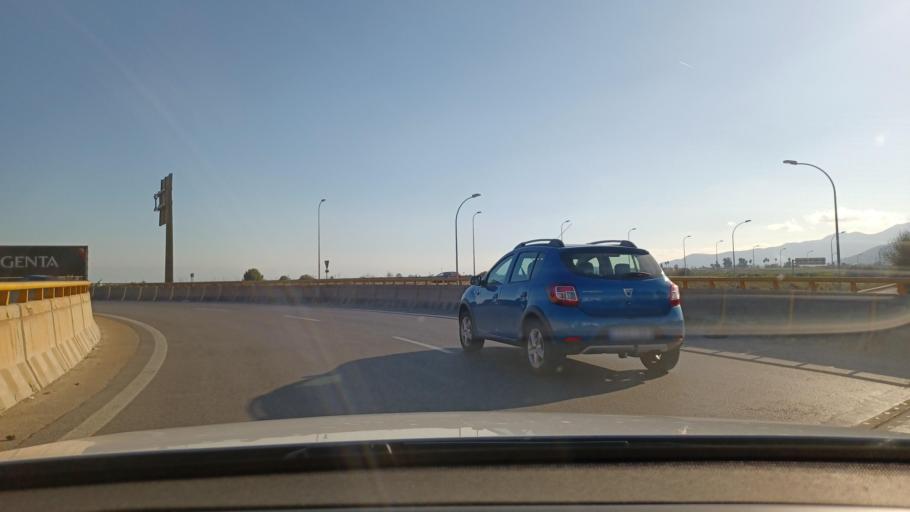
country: ES
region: Valencia
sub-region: Provincia de Castello
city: Betxi
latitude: 39.9495
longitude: -0.1797
